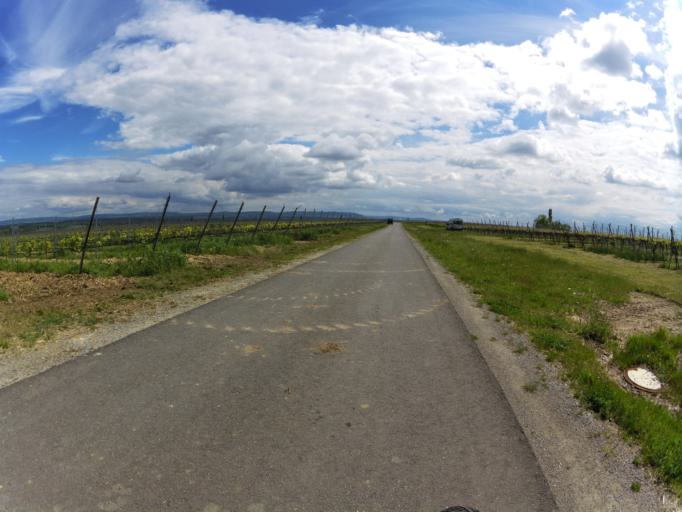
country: DE
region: Bavaria
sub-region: Regierungsbezirk Unterfranken
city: Sommerach
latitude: 49.8455
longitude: 10.1972
